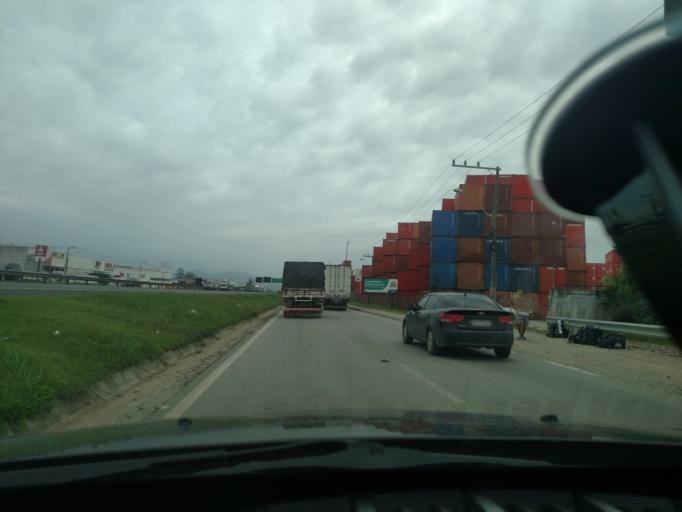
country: BR
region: Santa Catarina
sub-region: Itajai
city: Itajai
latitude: -26.8814
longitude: -48.7248
